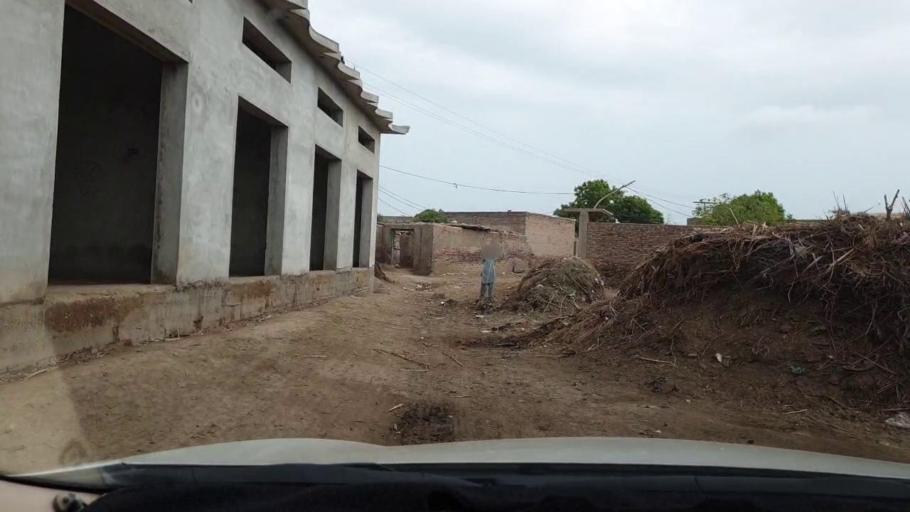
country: PK
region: Sindh
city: Tando Muhammad Khan
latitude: 25.1102
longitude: 68.6089
